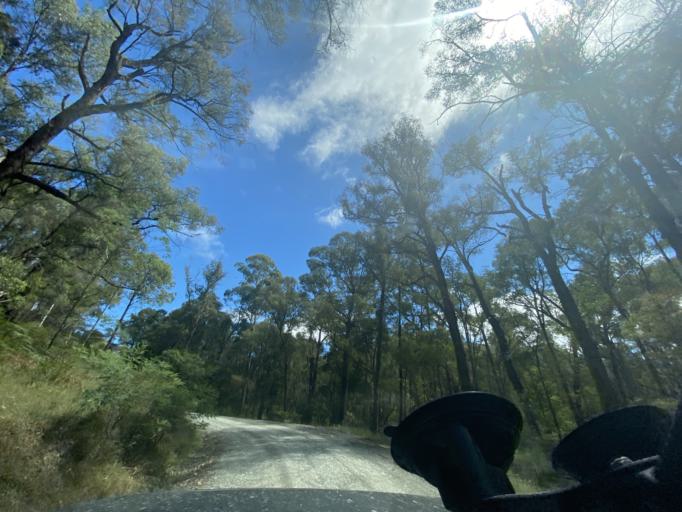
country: AU
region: Victoria
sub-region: Yarra Ranges
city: Millgrove
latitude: -37.5186
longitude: 146.0227
